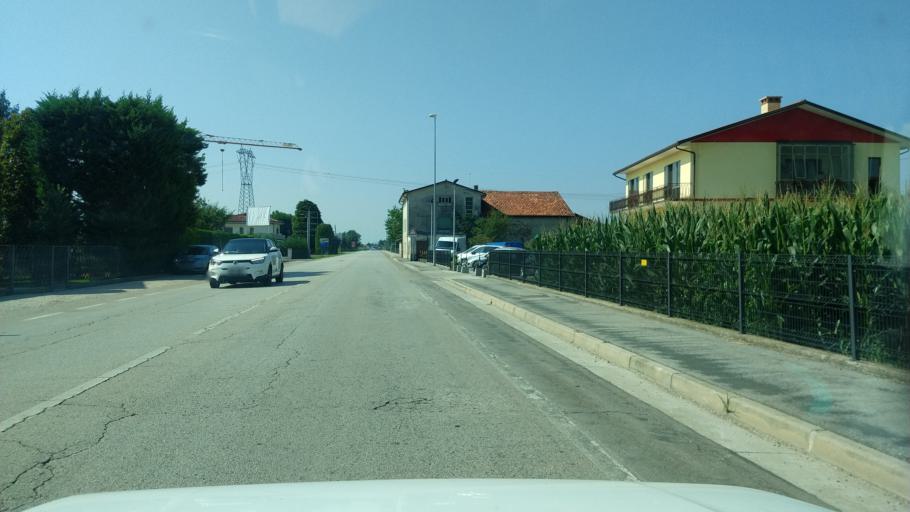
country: IT
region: Veneto
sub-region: Provincia di Vicenza
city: Schiavon
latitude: 45.6778
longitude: 11.6379
